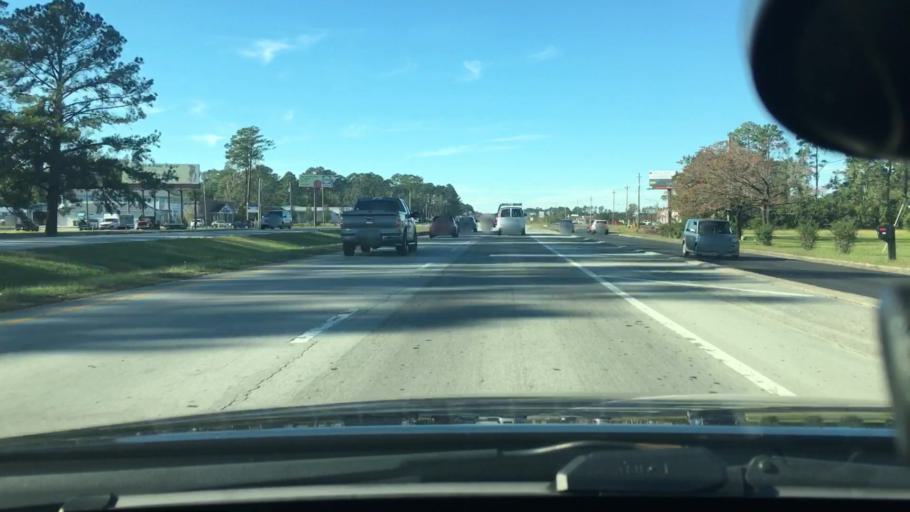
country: US
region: North Carolina
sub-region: Craven County
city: Havelock
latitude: 34.9005
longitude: -76.9302
